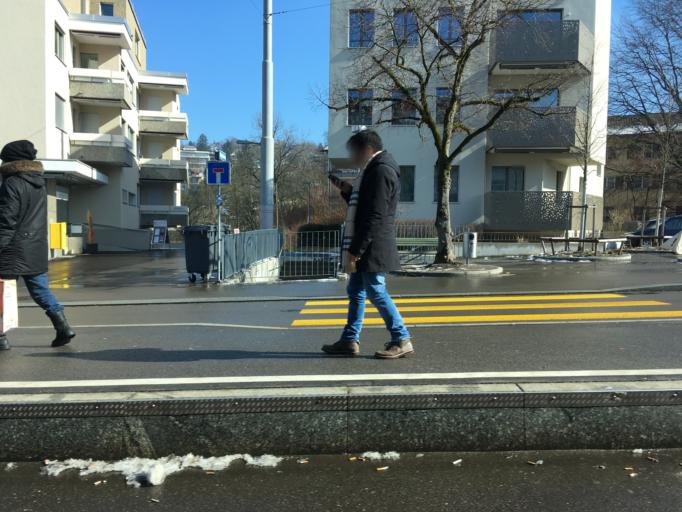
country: CH
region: Zurich
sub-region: Bezirk Zuerich
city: Zuerich (Kreis 8) / Weinegg
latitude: 47.3544
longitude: 8.5751
